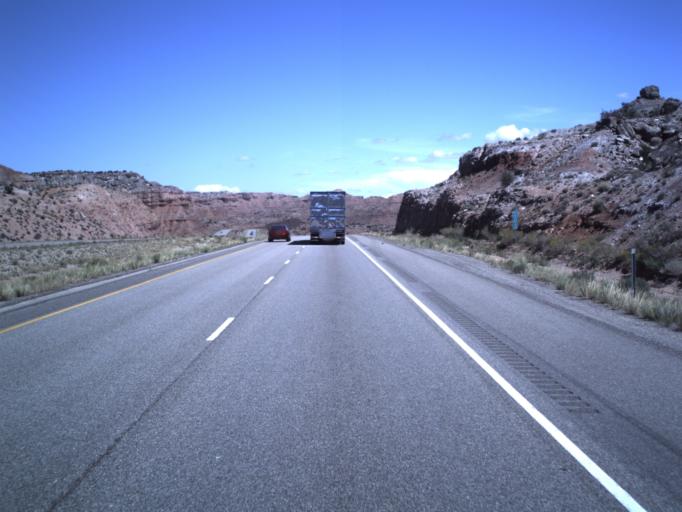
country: US
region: Utah
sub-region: Emery County
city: Ferron
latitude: 38.8225
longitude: -111.1486
